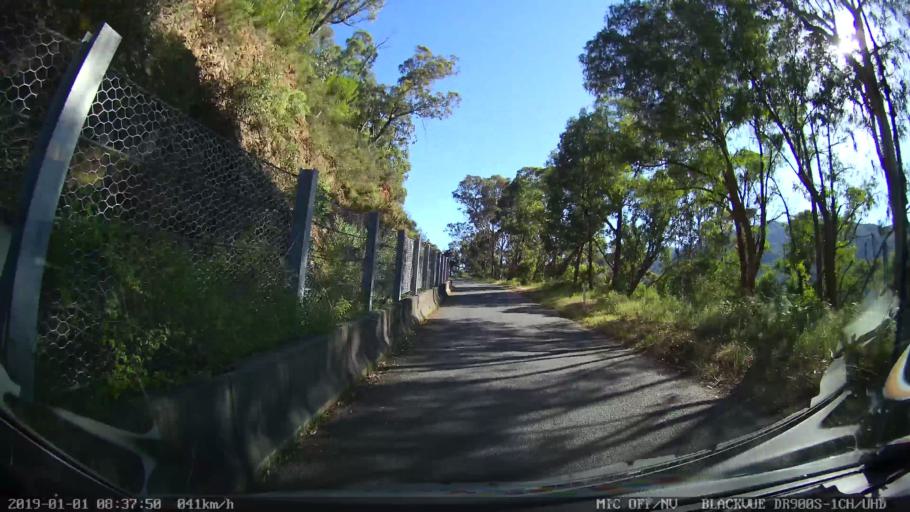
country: AU
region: New South Wales
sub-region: Snowy River
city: Jindabyne
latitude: -36.3360
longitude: 148.1968
